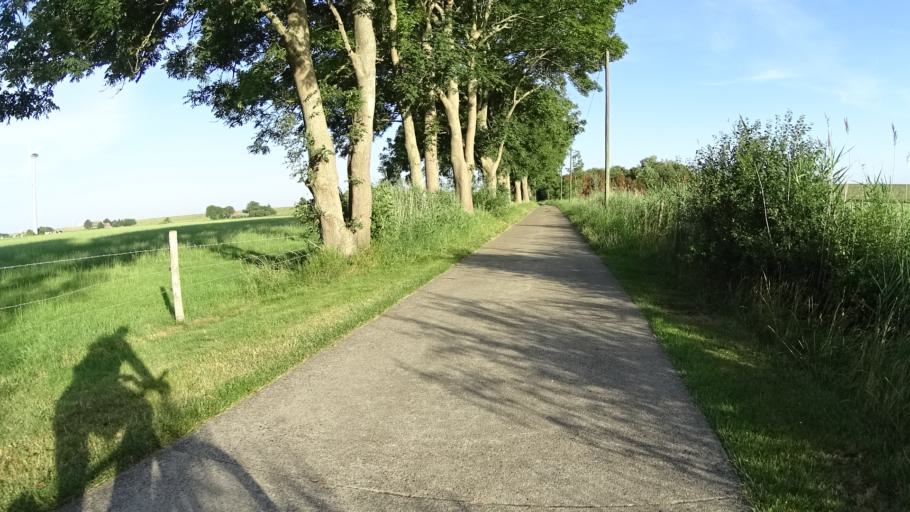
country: DE
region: Lower Saxony
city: Butjadingen
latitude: 53.6033
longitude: 8.2797
